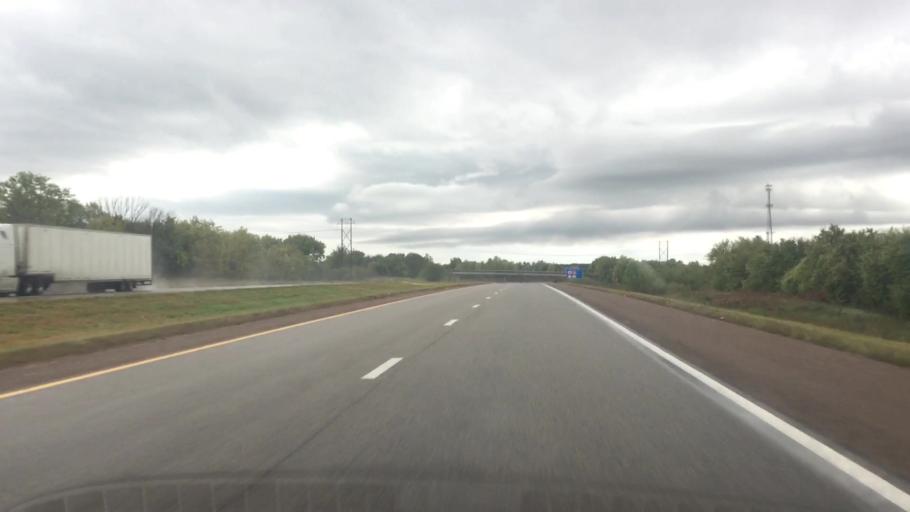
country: US
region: Kansas
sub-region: Miami County
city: Paola
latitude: 38.5902
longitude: -94.8355
